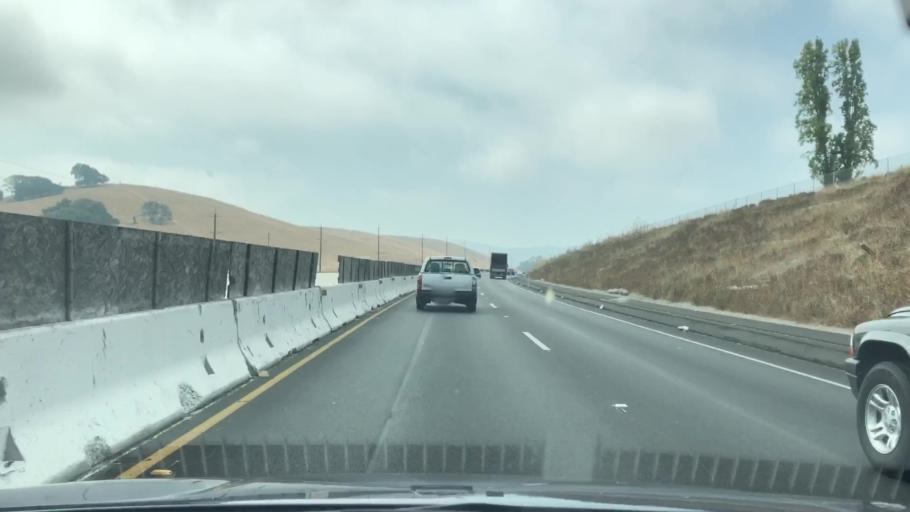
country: US
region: California
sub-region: Sonoma County
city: Petaluma
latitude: 38.2047
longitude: -122.5989
